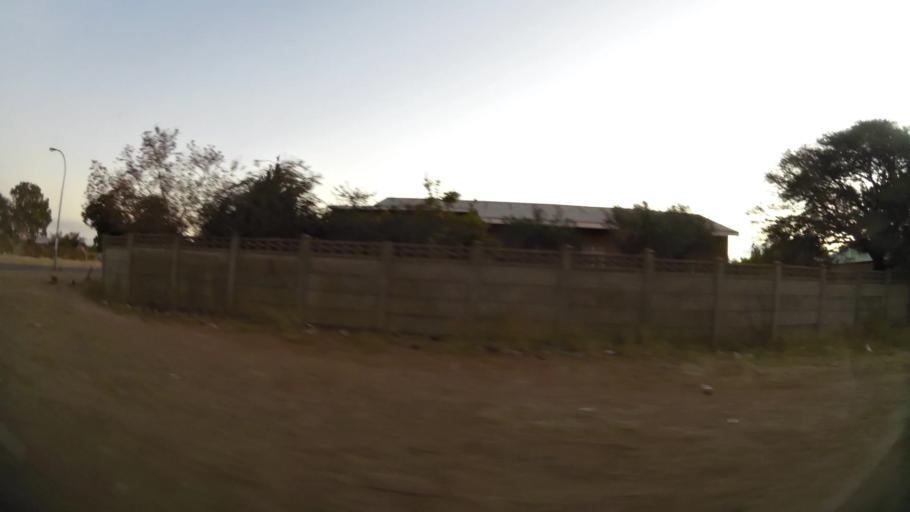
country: ZA
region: Northern Cape
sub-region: Frances Baard District Municipality
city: Kimberley
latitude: -28.7240
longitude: 24.7631
